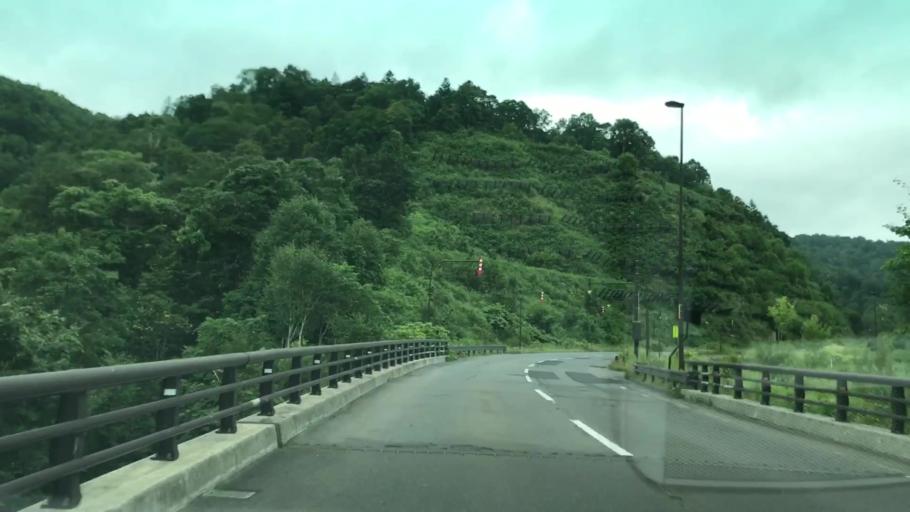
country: JP
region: Hokkaido
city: Otaru
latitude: 42.9916
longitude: 140.8762
